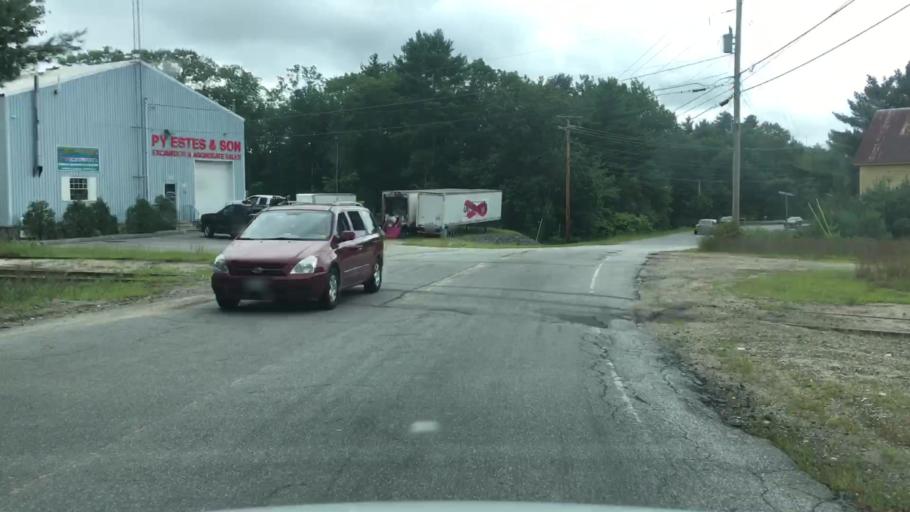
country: US
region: Maine
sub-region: York County
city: Cornish
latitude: 43.8084
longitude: -70.7787
